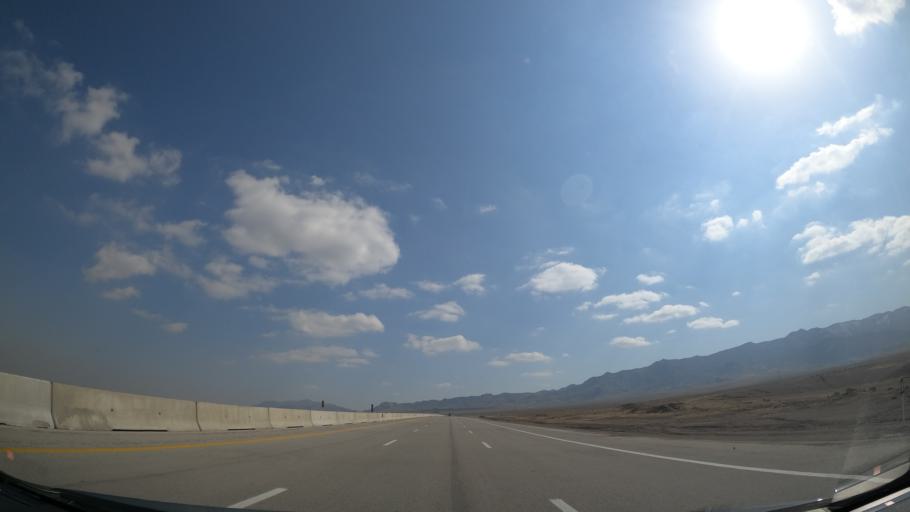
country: IR
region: Alborz
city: Eshtehard
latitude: 35.7243
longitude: 50.5655
